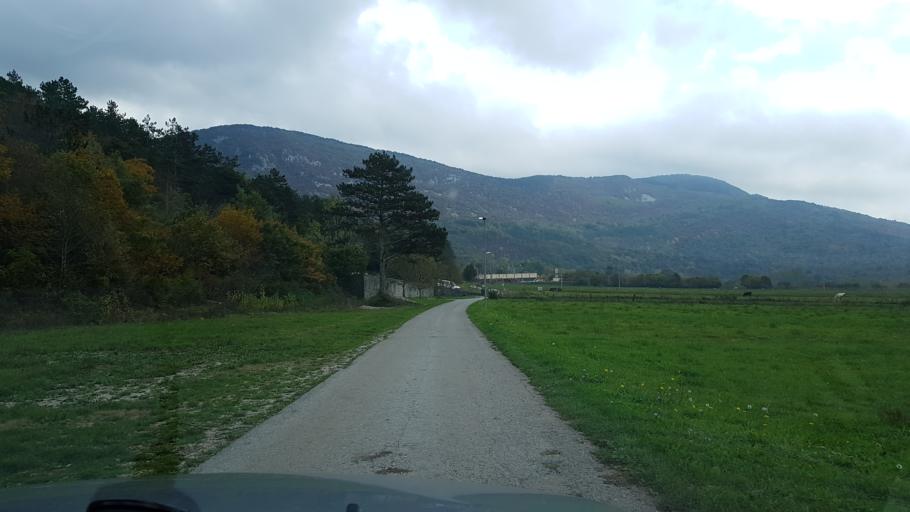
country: HR
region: Istarska
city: Buzet
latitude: 45.4088
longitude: 14.1077
